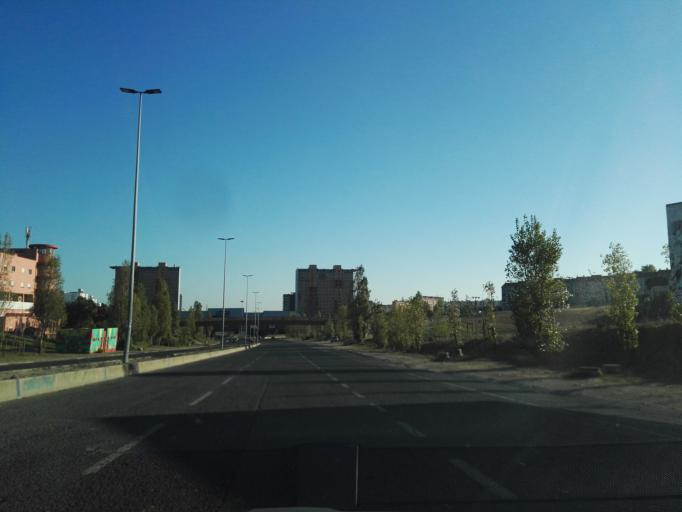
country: PT
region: Lisbon
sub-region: Loures
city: Moscavide
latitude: 38.7544
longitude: -9.1192
